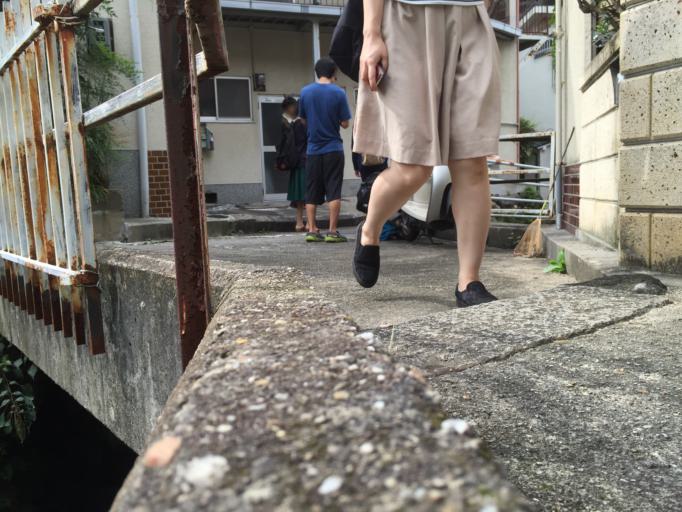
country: JP
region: Nara
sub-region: Ikoma-shi
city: Ikoma
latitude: 34.6905
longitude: 135.6956
